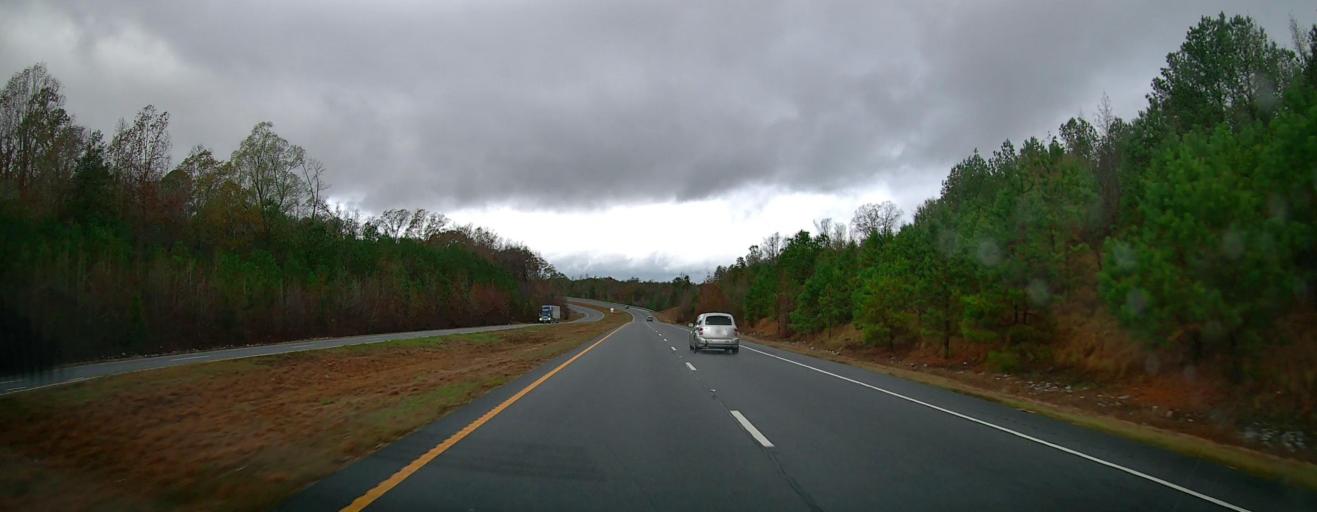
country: US
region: Georgia
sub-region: Jackson County
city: Nicholson
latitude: 34.0552
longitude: -83.4102
